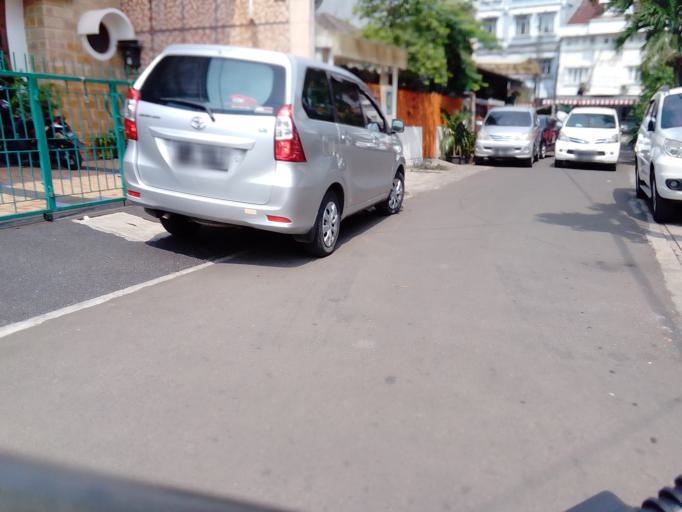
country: ID
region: Jakarta Raya
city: Jakarta
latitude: -6.2097
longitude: 106.8117
